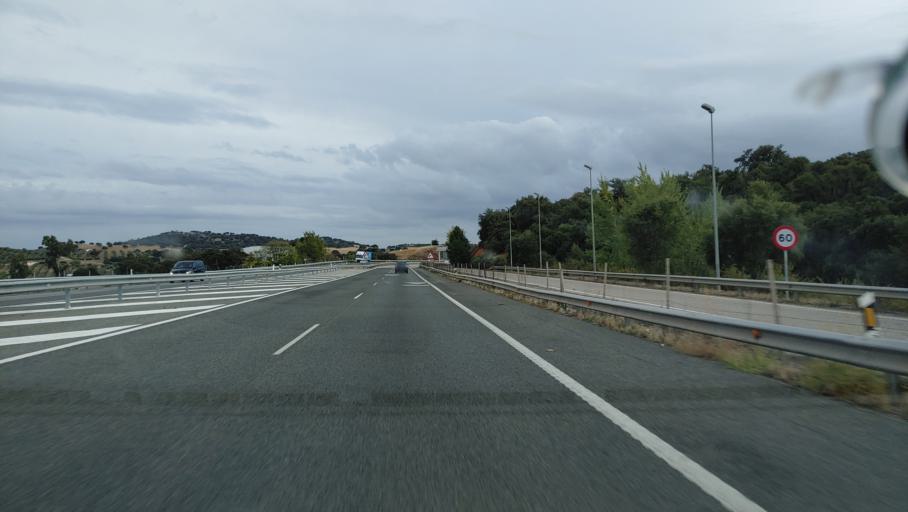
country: ES
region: Andalusia
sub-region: Provincia de Jaen
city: Santa Elena
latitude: 38.3360
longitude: -3.5438
